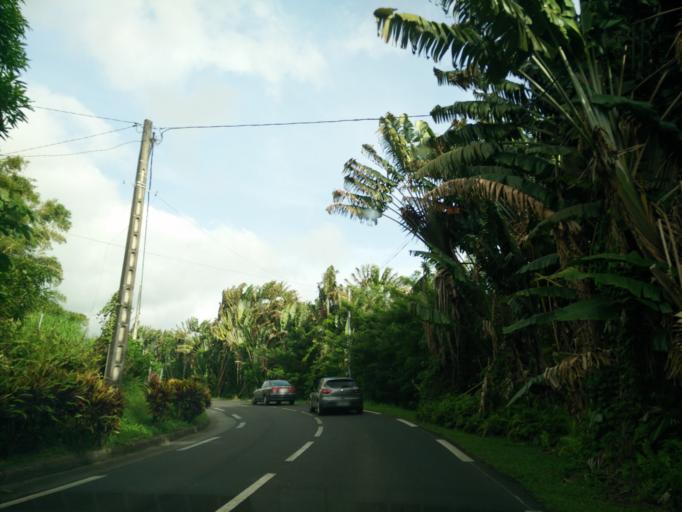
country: MQ
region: Martinique
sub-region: Martinique
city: Le Morne-Rouge
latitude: 14.7621
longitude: -61.1544
